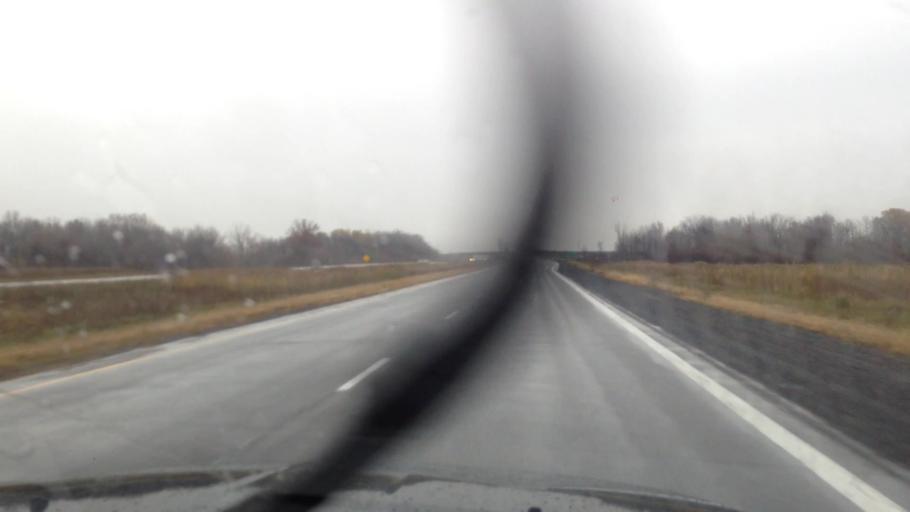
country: CA
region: Ontario
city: Casselman
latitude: 45.3385
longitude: -74.9106
